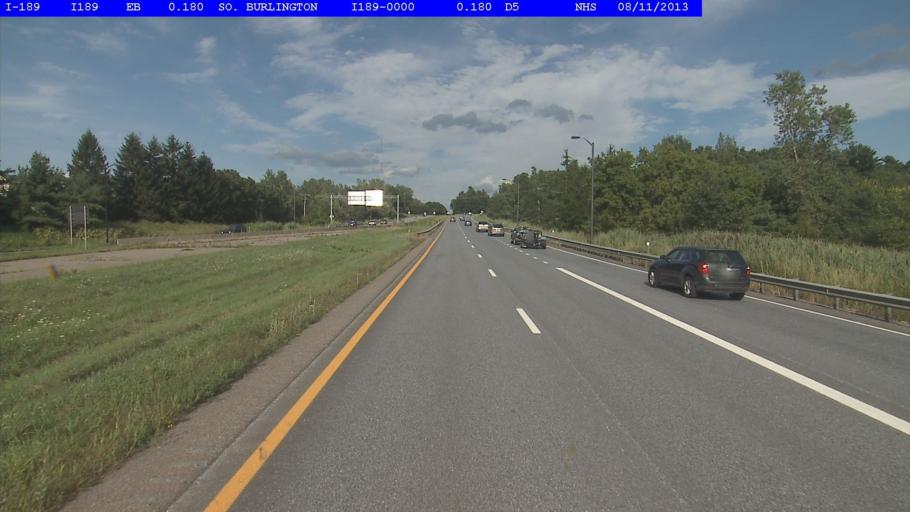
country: US
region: Vermont
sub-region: Chittenden County
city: Burlington
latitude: 44.4478
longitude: -73.2061
